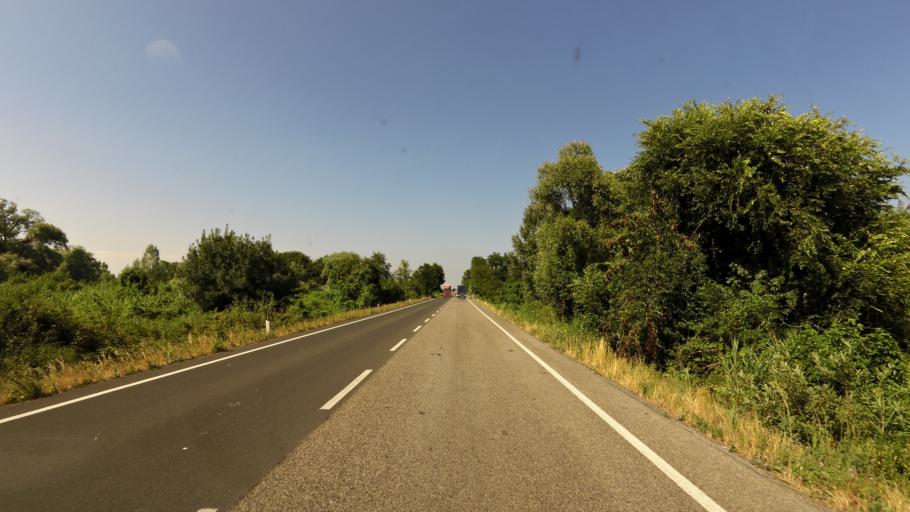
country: IT
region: Emilia-Romagna
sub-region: Provincia di Ravenna
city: Marina Romea
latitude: 44.5443
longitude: 12.2373
